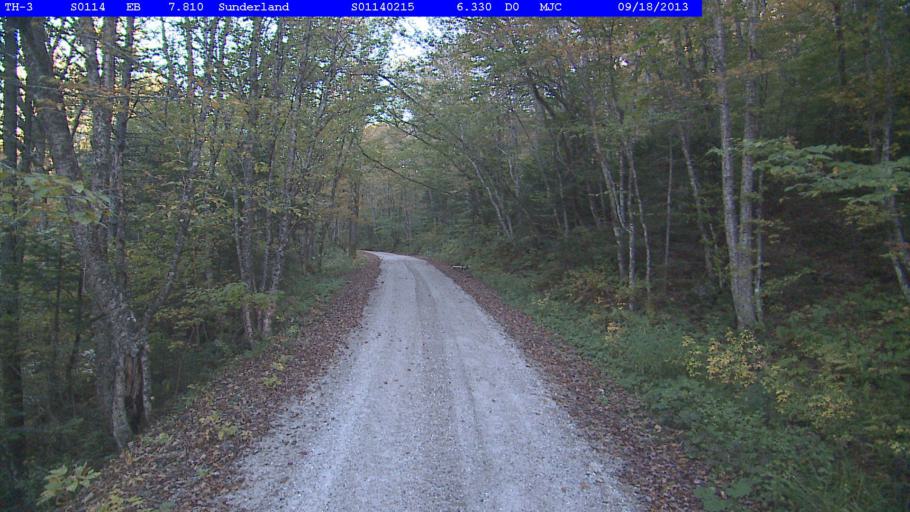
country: US
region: Vermont
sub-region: Bennington County
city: Arlington
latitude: 43.0551
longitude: -73.0615
